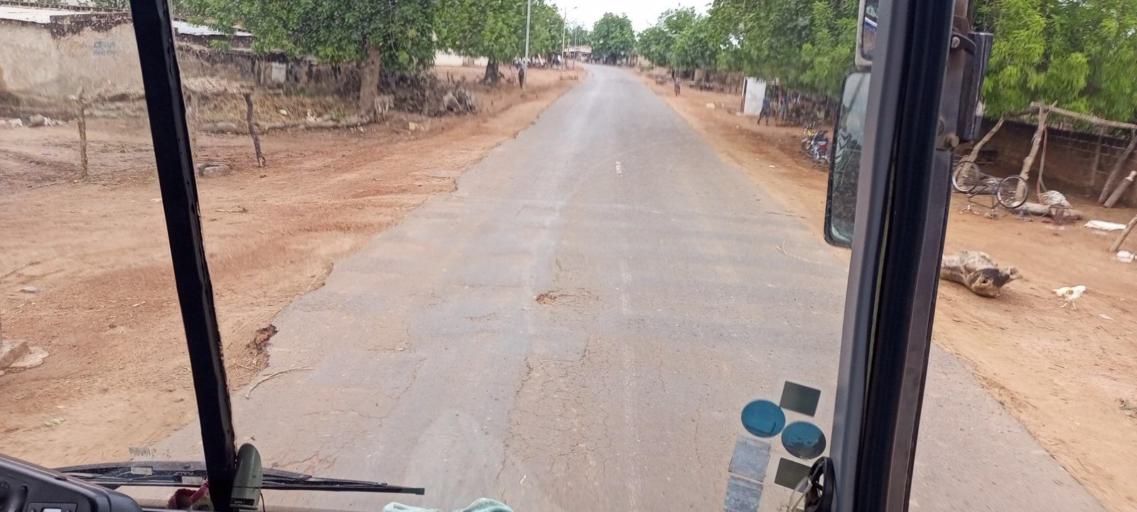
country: ML
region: Segou
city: Bla
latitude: 12.6709
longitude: -5.7207
